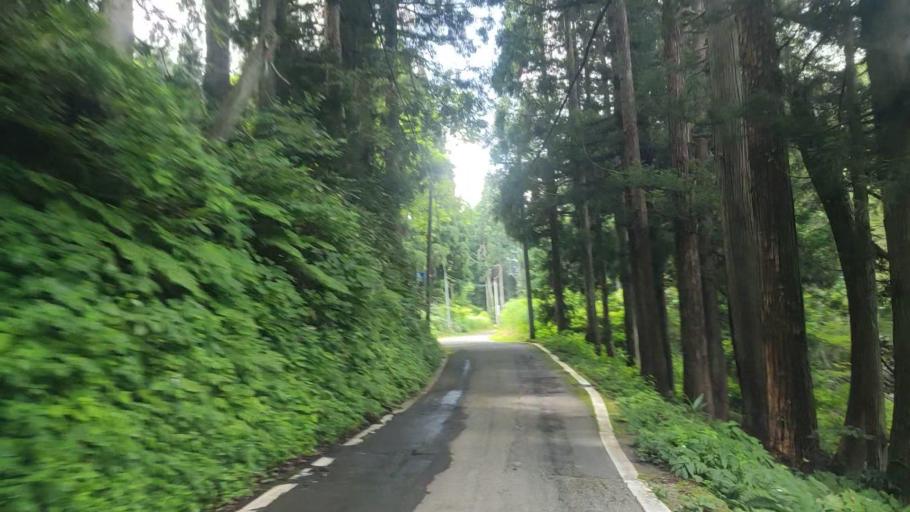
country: JP
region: Fukui
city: Katsuyama
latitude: 36.2053
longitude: 136.5260
